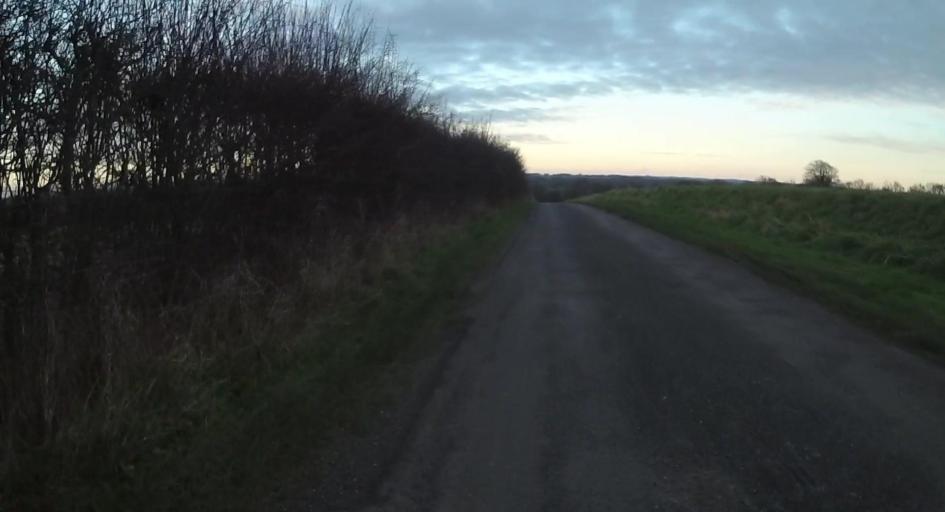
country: GB
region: England
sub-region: Hampshire
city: Swanmore
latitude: 51.0154
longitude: -1.1413
